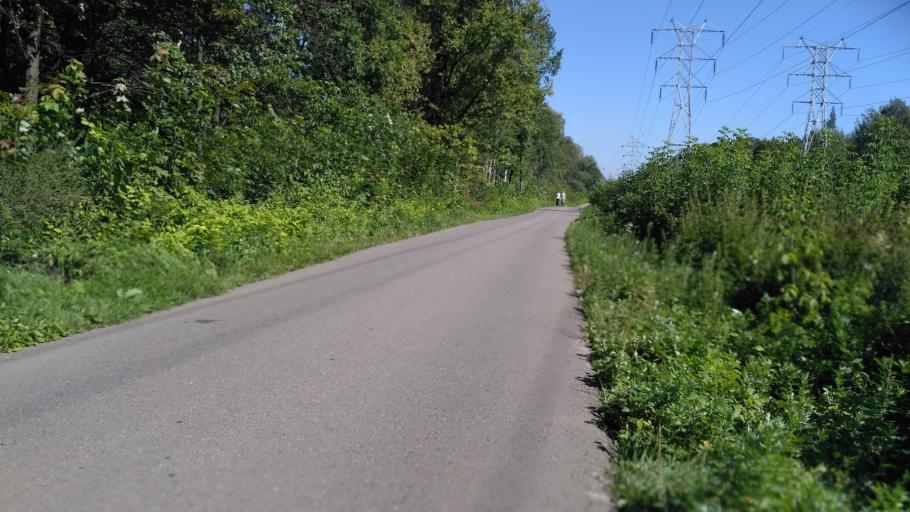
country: RU
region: Moscow
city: Metrogorodok
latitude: 55.7804
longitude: 37.7549
